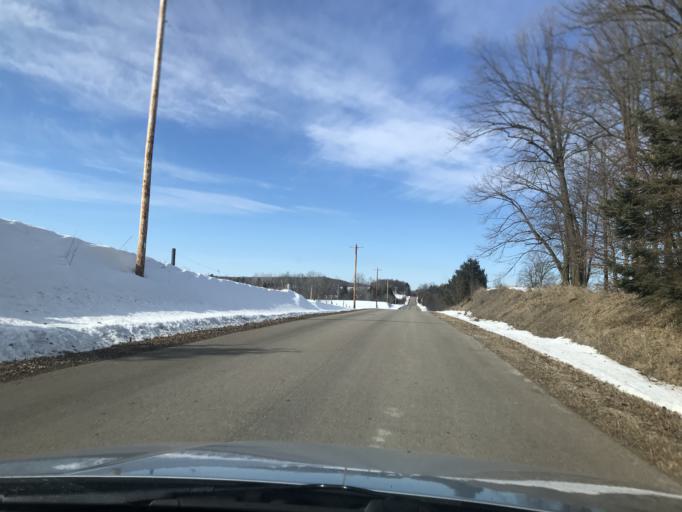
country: US
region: Wisconsin
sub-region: Oconto County
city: Gillett
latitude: 44.9617
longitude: -88.2898
